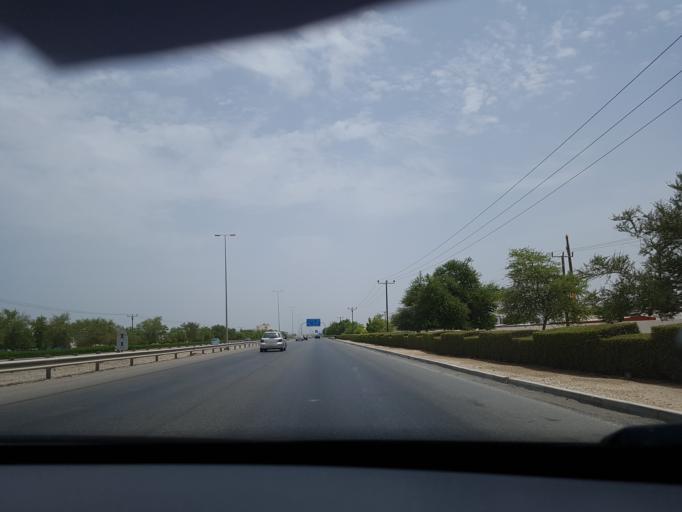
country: OM
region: Al Batinah
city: Barka'
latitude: 23.6798
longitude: 58.0070
